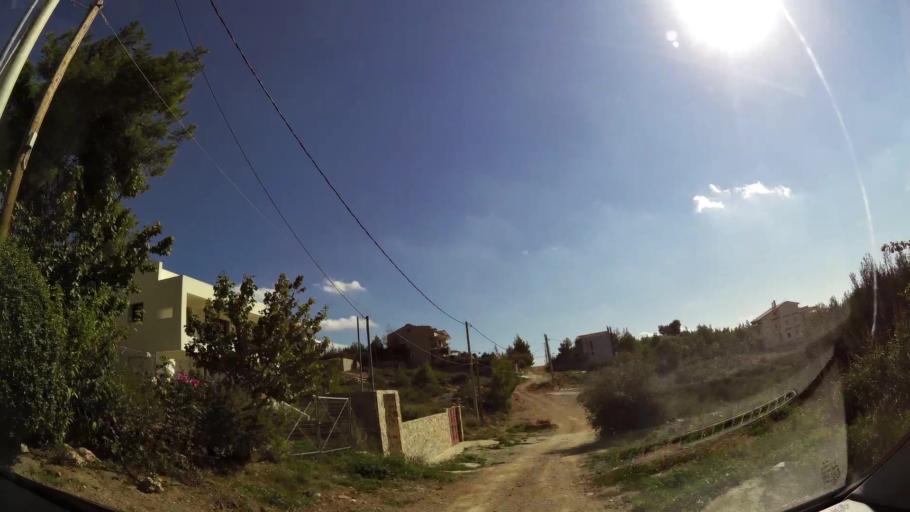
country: GR
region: Attica
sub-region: Nomarchia Anatolikis Attikis
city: Dioni
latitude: 38.0323
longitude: 23.9219
